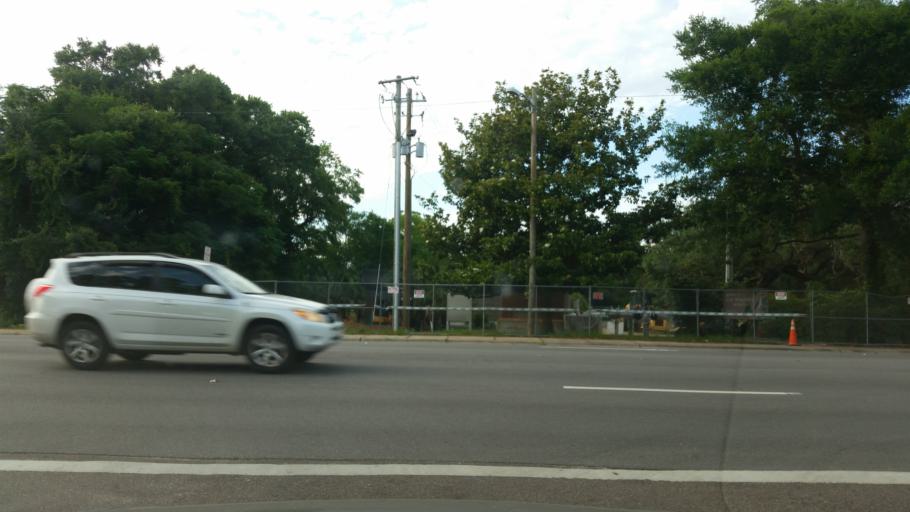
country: US
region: Florida
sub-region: Escambia County
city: East Pensacola Heights
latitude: 30.4254
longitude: -87.1865
